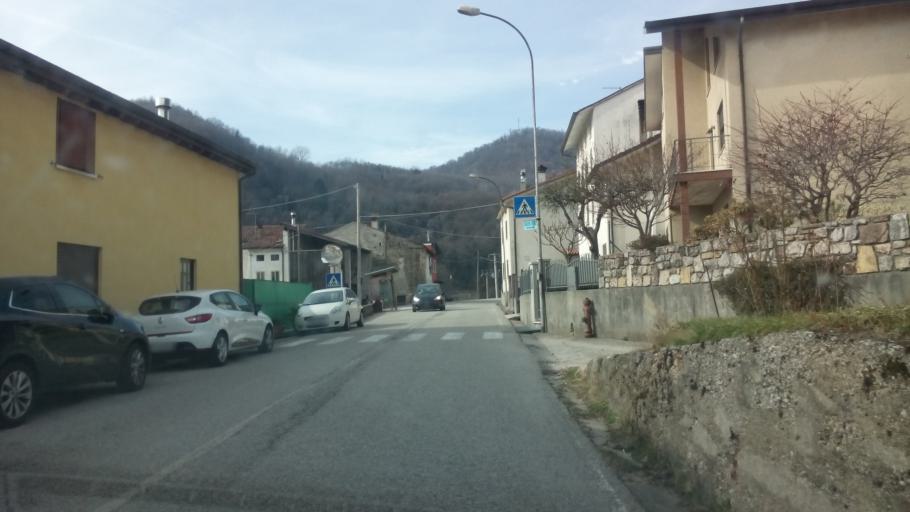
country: IT
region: Veneto
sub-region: Provincia di Vicenza
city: Schio
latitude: 45.7404
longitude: 11.3534
